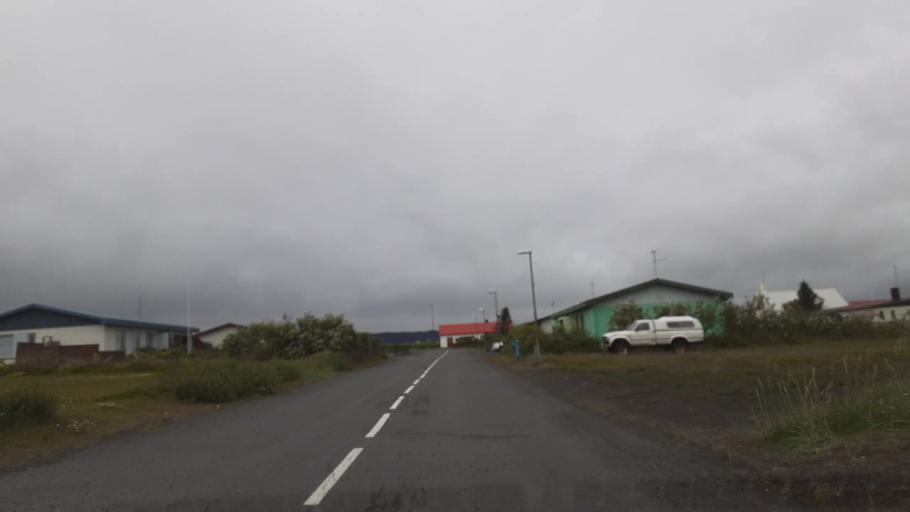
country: IS
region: Northeast
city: Husavik
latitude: 66.3030
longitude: -16.4474
